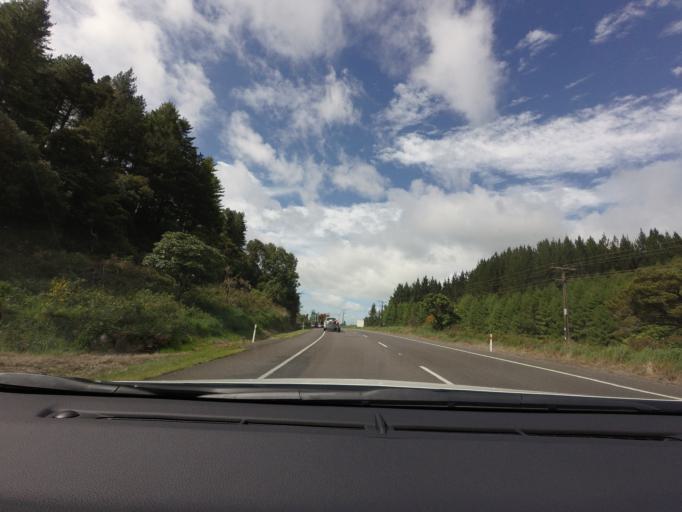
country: NZ
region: Bay of Plenty
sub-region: Rotorua District
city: Rotorua
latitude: -38.3264
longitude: 176.3694
